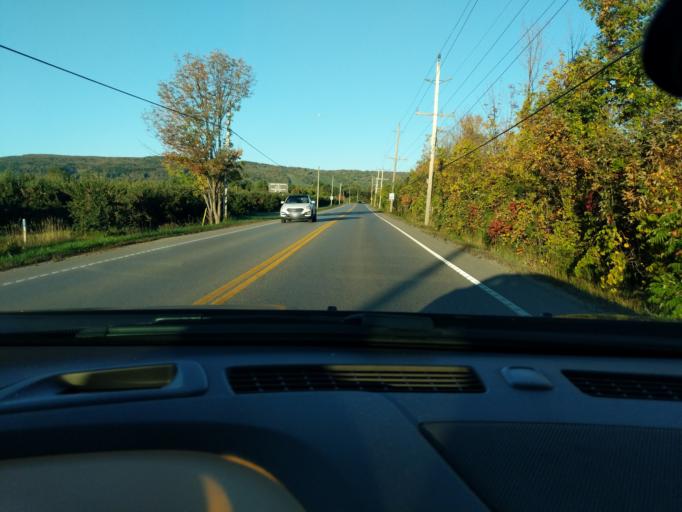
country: CA
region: Ontario
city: Collingwood
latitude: 44.4984
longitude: -80.2707
